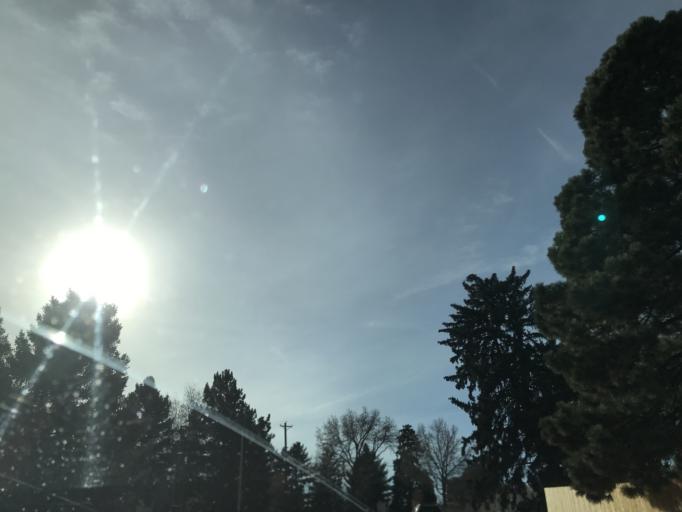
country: US
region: Colorado
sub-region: Arapahoe County
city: Littleton
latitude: 39.5991
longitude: -105.0117
